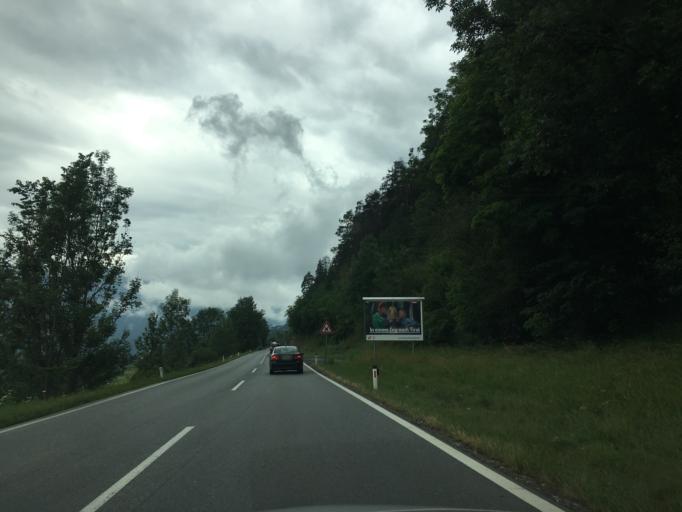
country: AT
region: Tyrol
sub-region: Politischer Bezirk Imst
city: Imst
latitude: 47.2556
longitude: 10.7513
